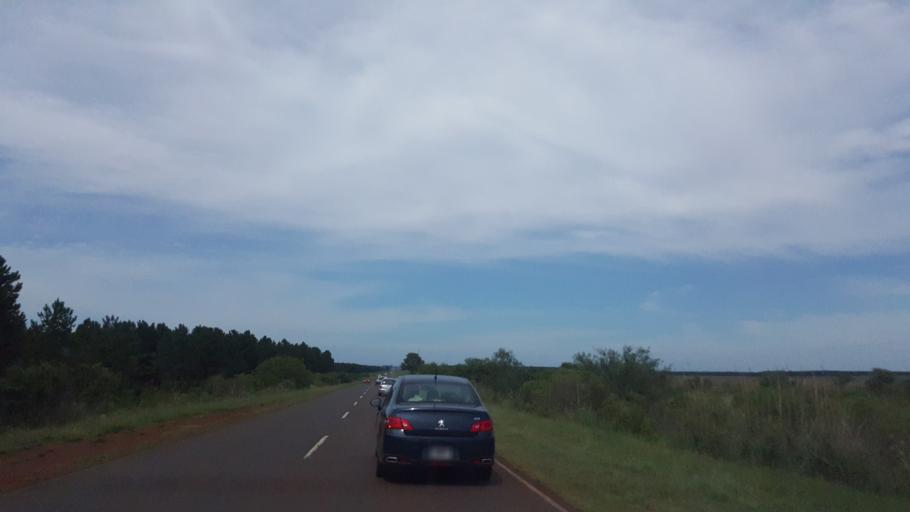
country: PY
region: Itapua
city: San Juan del Parana
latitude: -27.5075
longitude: -56.1290
